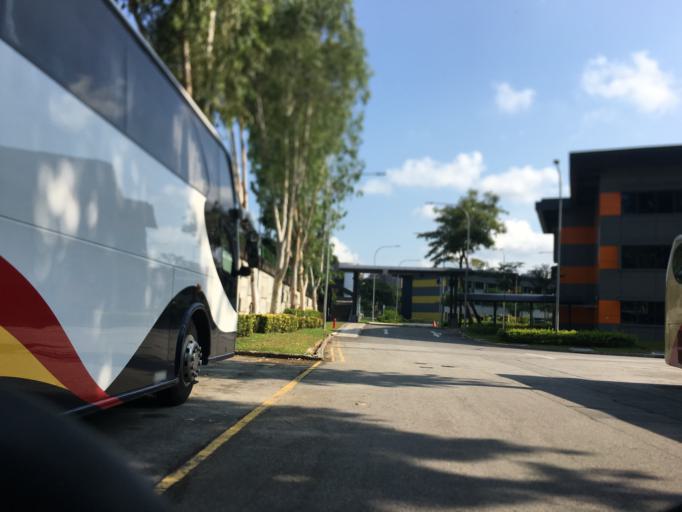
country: SG
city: Singapore
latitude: 1.2968
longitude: 103.7860
